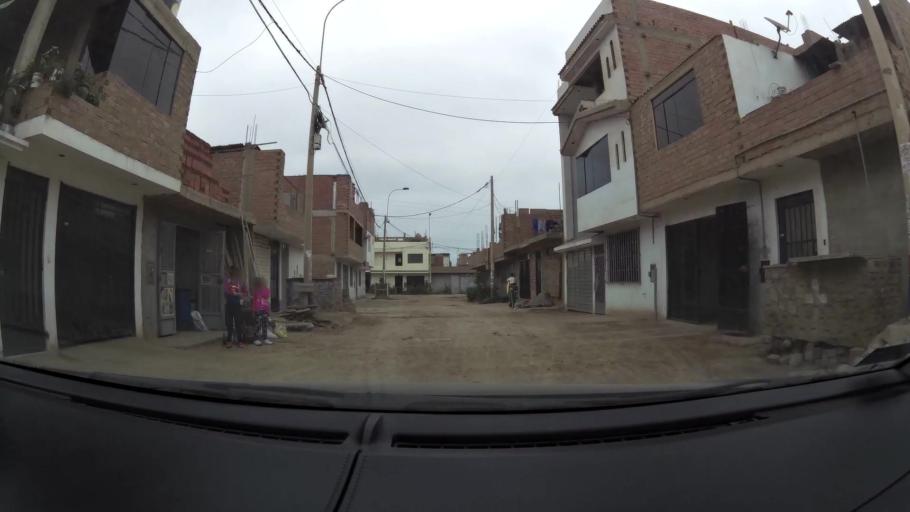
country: PE
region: Lima
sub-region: Lima
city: Independencia
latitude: -11.9612
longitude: -77.0973
